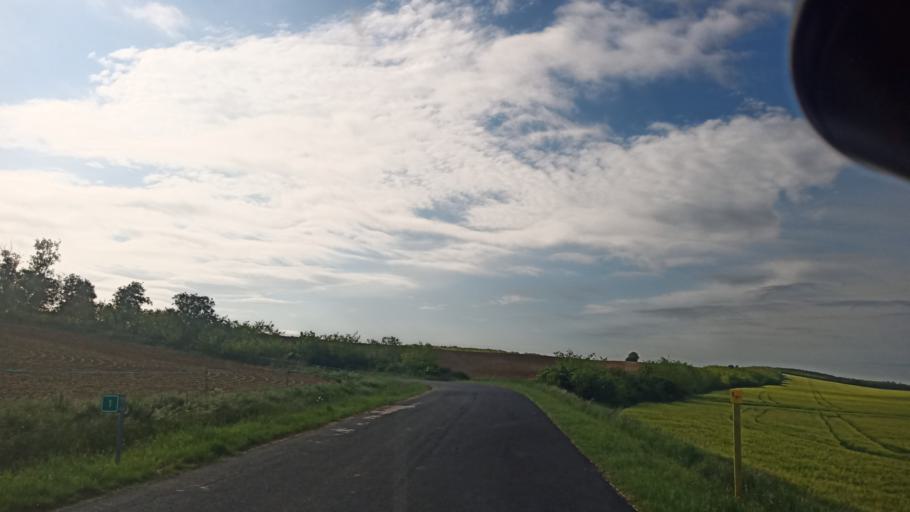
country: HU
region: Zala
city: Pacsa
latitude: 46.7040
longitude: 17.0528
